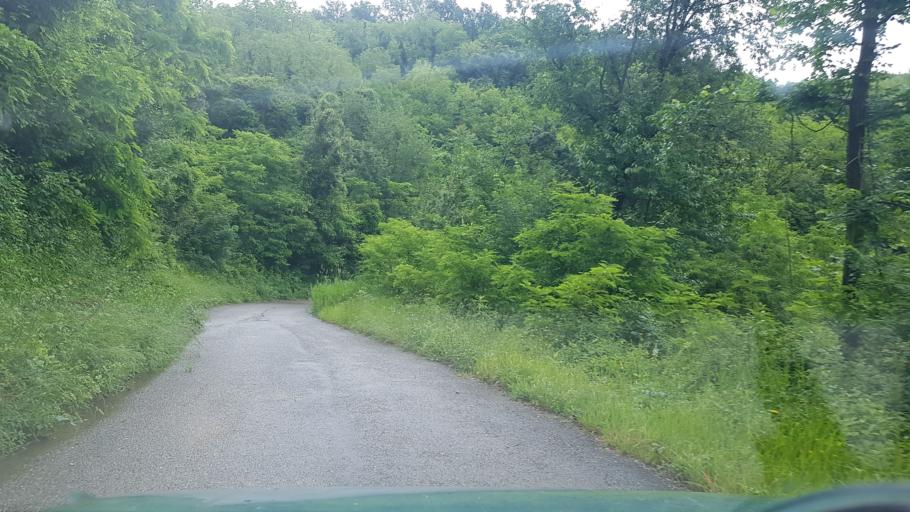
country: IT
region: Friuli Venezia Giulia
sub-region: Provincia di Gorizia
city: San Floriano del Collio
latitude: 45.9505
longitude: 13.5853
